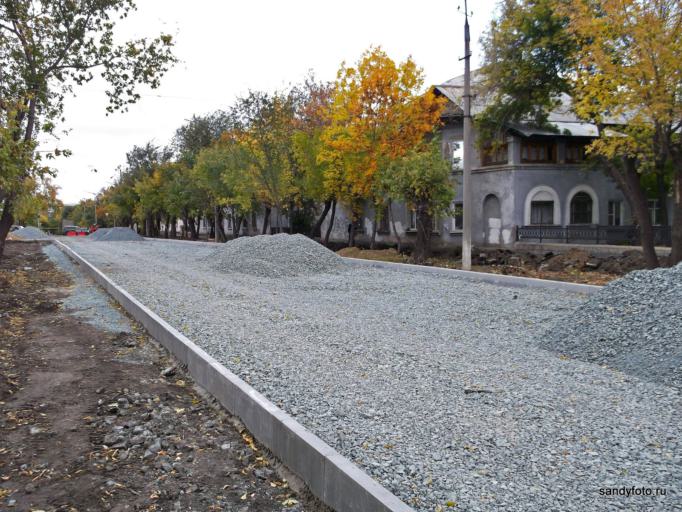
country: RU
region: Chelyabinsk
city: Troitsk
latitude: 54.0887
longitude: 61.5551
